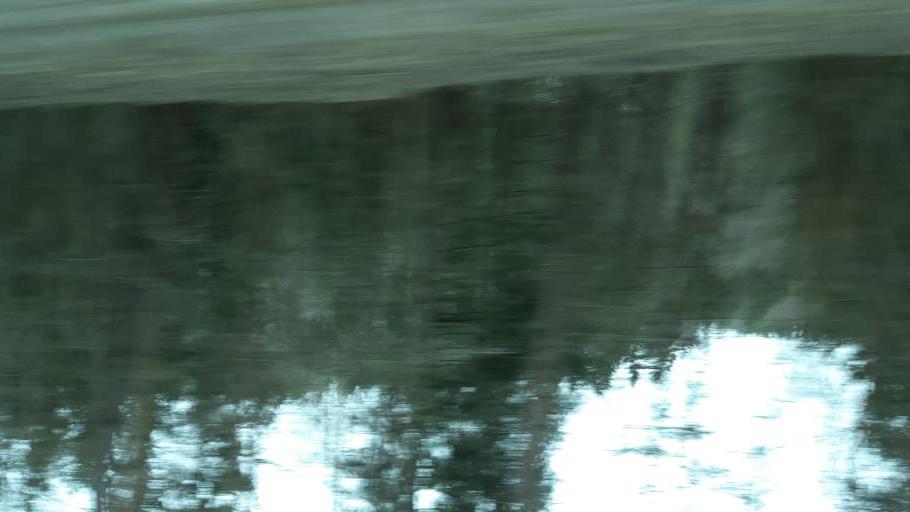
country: PL
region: Podlasie
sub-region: Suwalki
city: Suwalki
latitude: 54.2848
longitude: 22.9505
